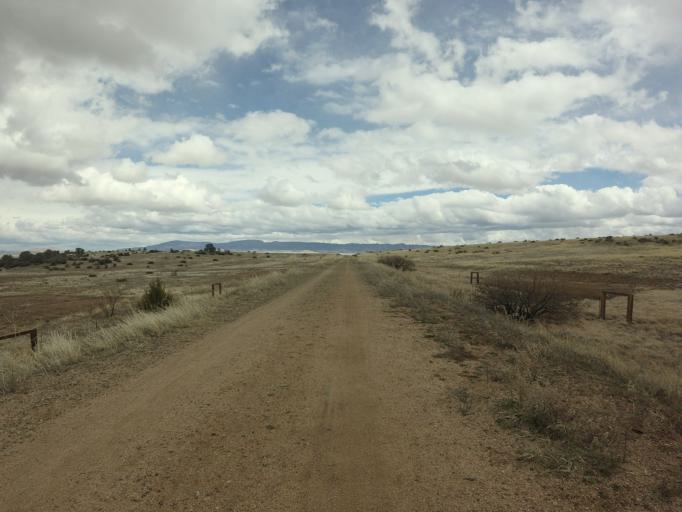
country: US
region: Arizona
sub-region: Yavapai County
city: Prescott Valley
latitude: 34.6111
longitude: -112.3814
